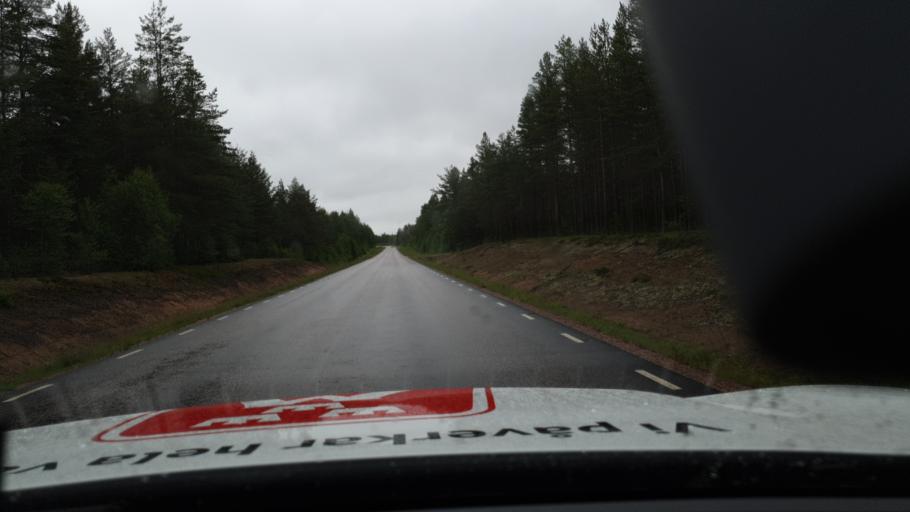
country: SE
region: Norrbotten
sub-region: Overtornea Kommun
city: OEvertornea
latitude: 66.4761
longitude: 23.6846
